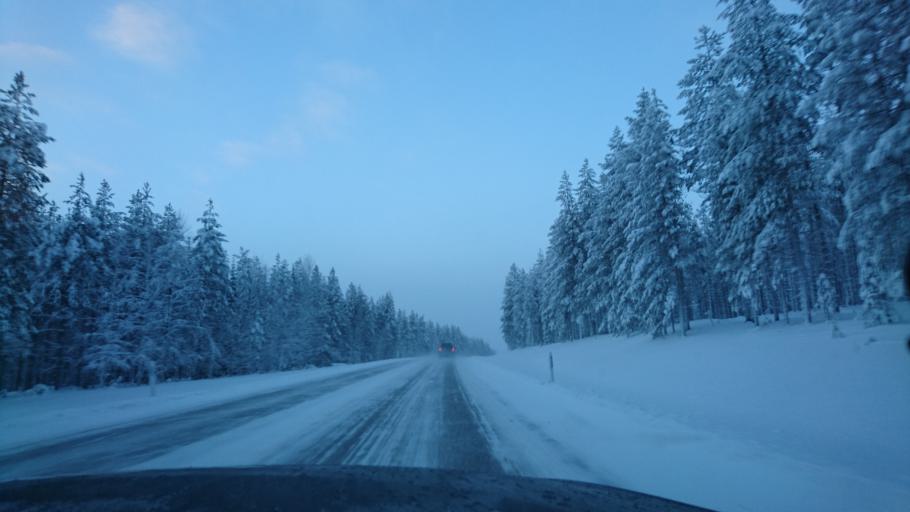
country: FI
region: Northern Ostrobothnia
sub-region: Koillismaa
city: Taivalkoski
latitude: 65.4764
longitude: 27.7795
